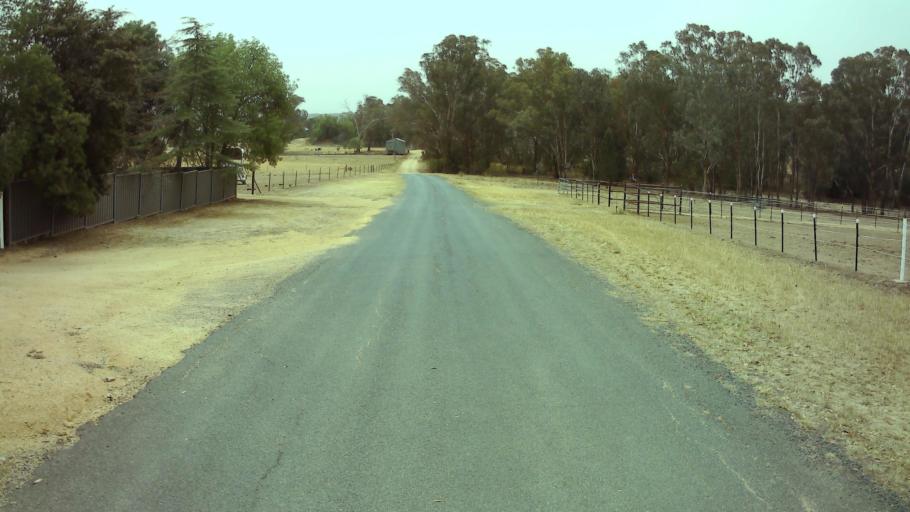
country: AU
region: New South Wales
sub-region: Weddin
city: Grenfell
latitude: -33.9062
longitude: 148.1540
